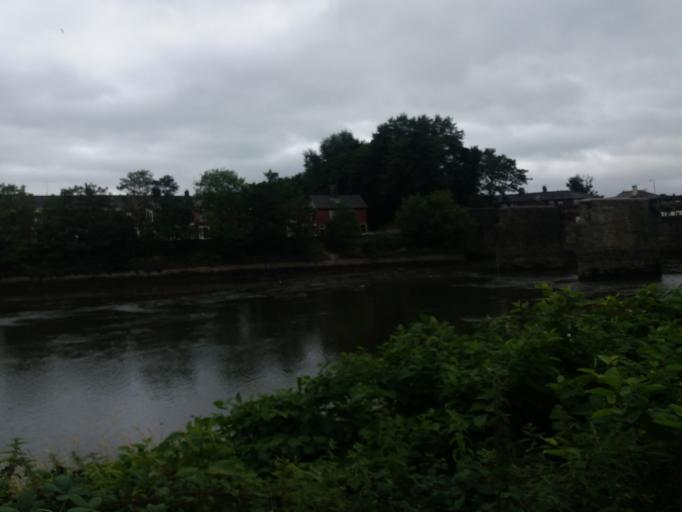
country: GB
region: England
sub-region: Lancashire
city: Preston
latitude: 53.7487
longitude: -2.7123
